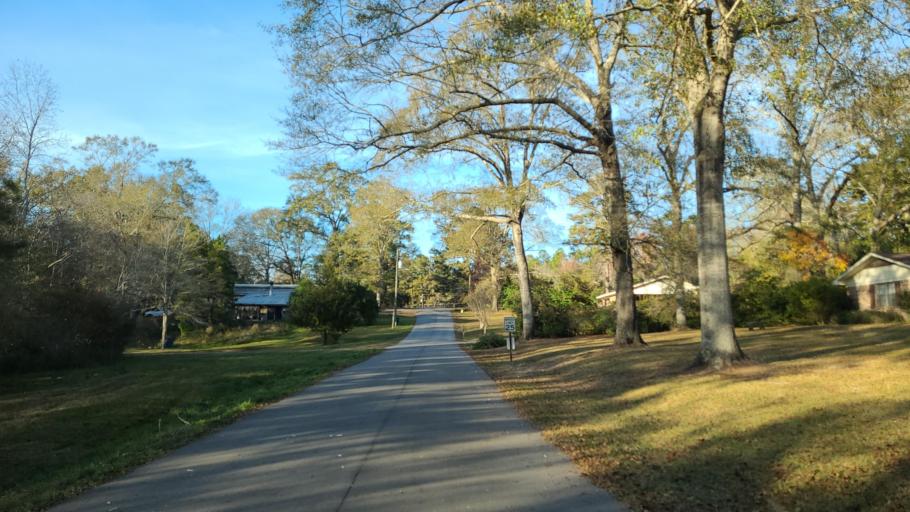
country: US
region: Mississippi
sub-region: Lamar County
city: Purvis
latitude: 31.1436
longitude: -89.4196
